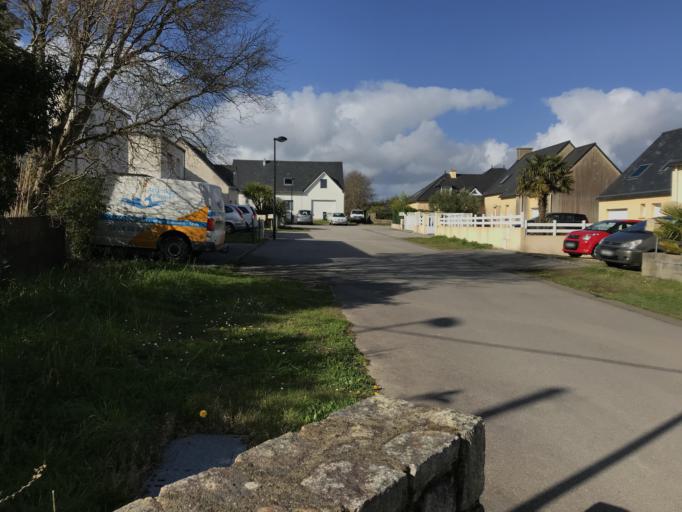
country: FR
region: Brittany
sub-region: Departement du Finistere
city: Plougastel-Daoulas
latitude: 48.3814
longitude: -4.3461
